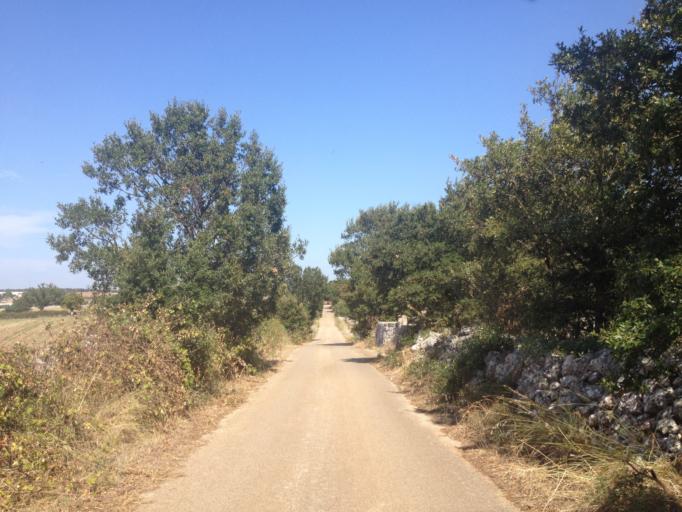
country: IT
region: Apulia
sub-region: Provincia di Bari
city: Gioia del Colle
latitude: 40.8228
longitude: 17.0101
